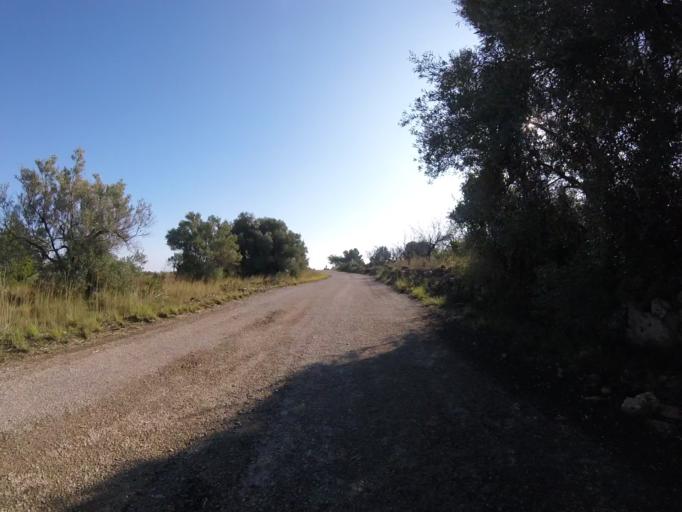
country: ES
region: Valencia
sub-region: Provincia de Castello
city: Peniscola
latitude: 40.3889
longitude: 0.3718
